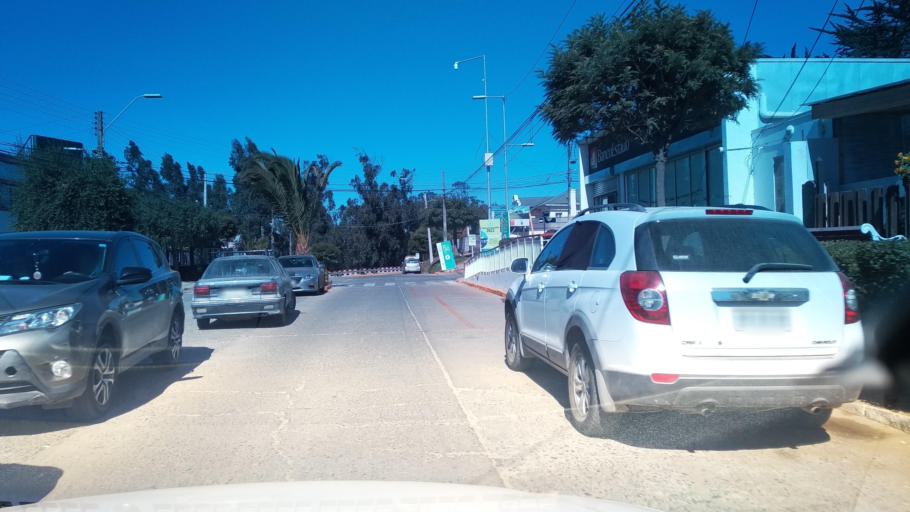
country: CL
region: O'Higgins
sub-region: Provincia de Colchagua
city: Santa Cruz
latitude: -34.3888
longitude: -72.0017
